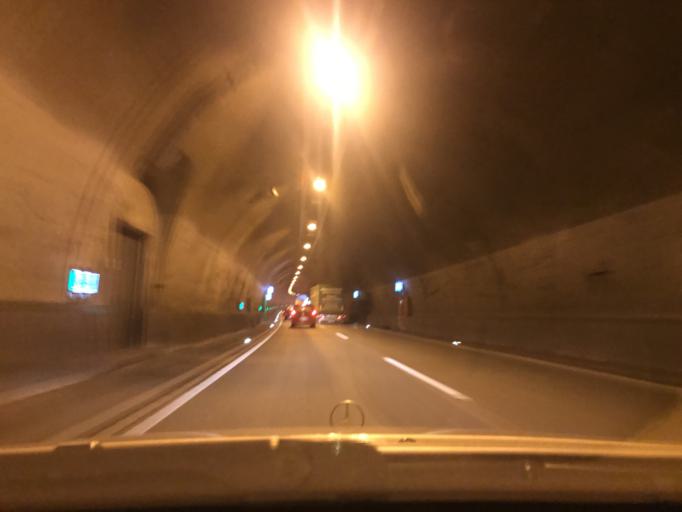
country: DE
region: North Rhine-Westphalia
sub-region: Regierungsbezirk Arnsberg
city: Bochum
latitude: 51.4620
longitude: 7.1997
